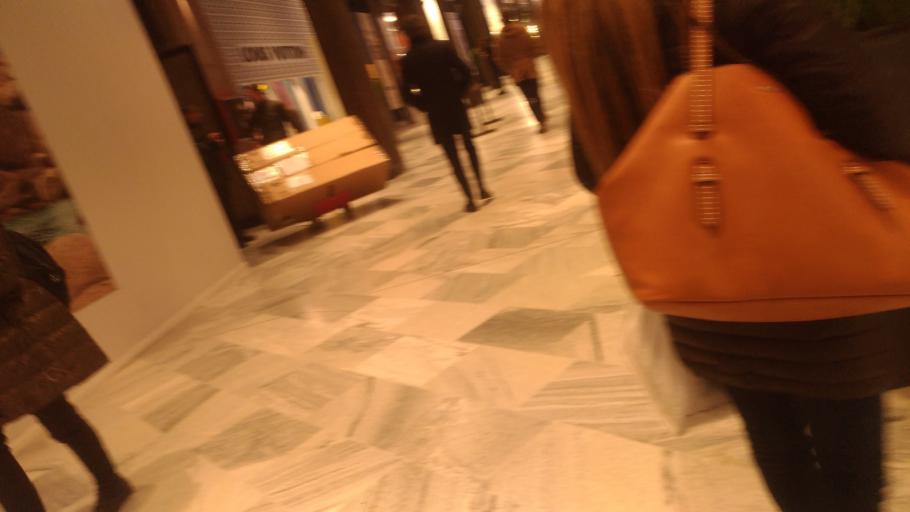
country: IT
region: Emilia-Romagna
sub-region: Provincia di Bologna
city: Bologna
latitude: 44.4915
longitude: 11.3441
